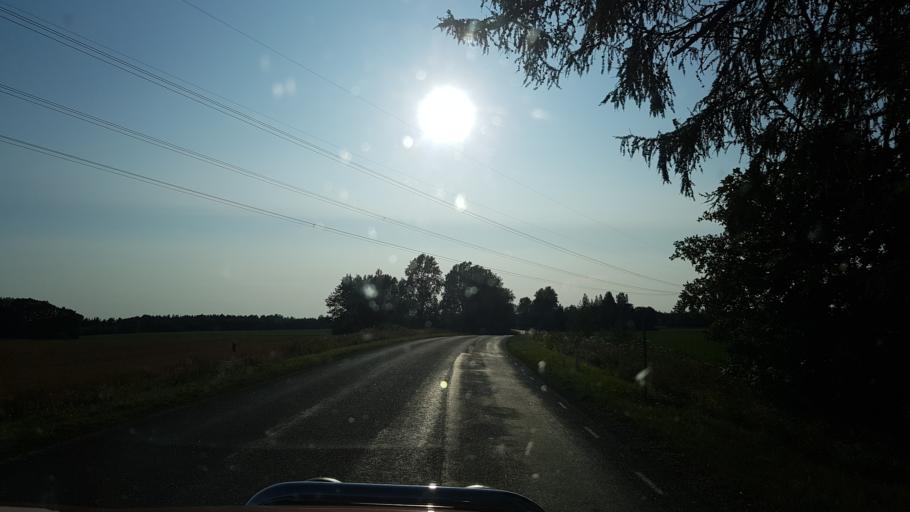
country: EE
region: Raplamaa
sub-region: Kehtna vald
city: Kehtna
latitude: 59.0544
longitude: 24.9965
